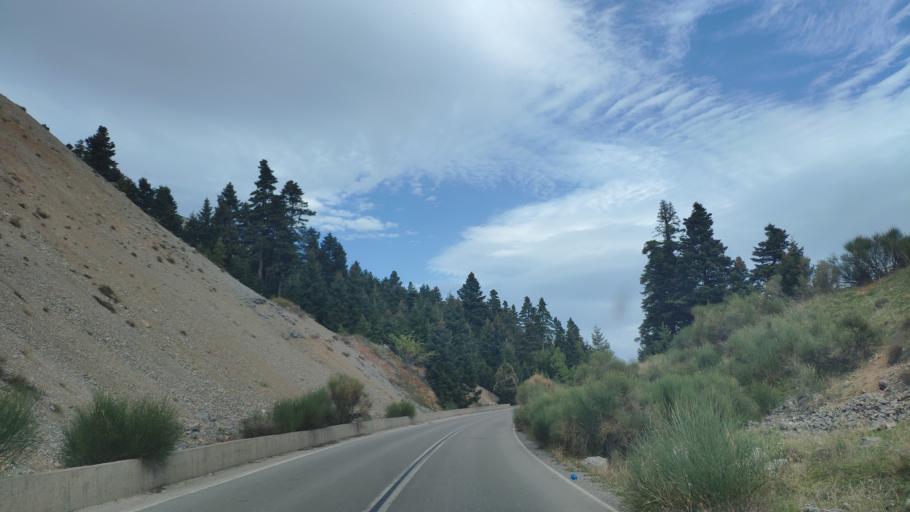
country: GR
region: Central Greece
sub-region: Nomos Fokidos
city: Amfissa
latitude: 38.6490
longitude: 22.3847
